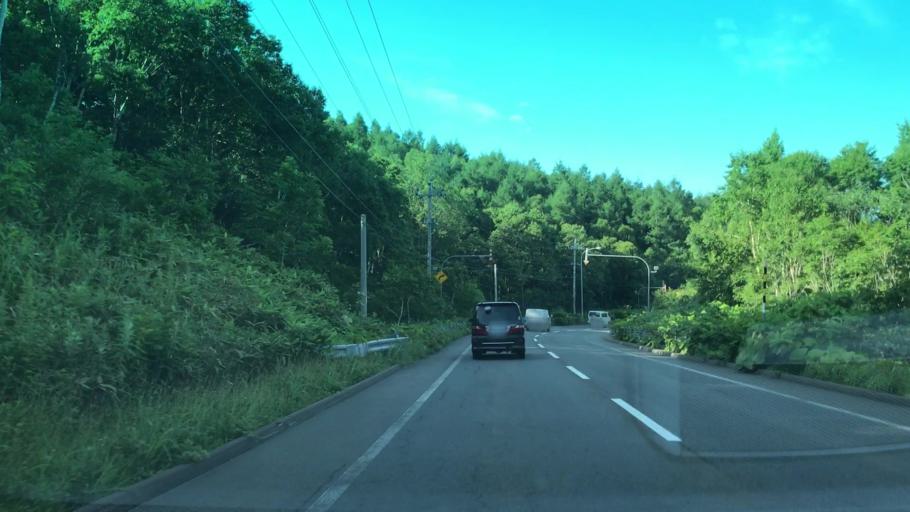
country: JP
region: Hokkaido
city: Otaru
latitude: 43.1084
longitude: 141.0050
